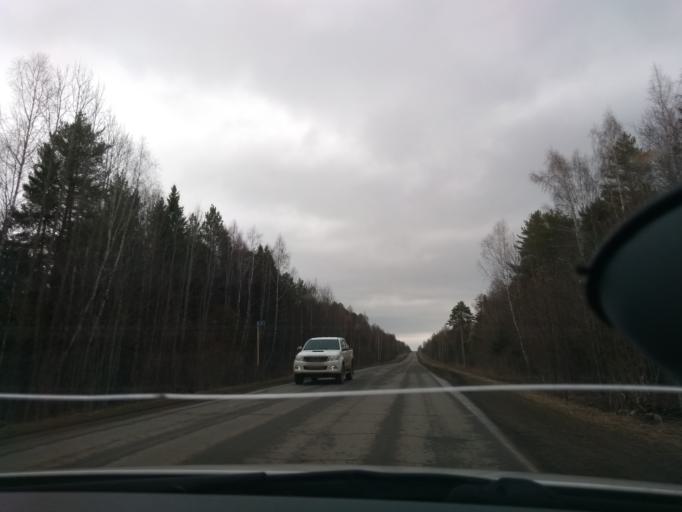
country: RU
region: Perm
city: Kungur
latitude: 57.3600
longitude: 56.8153
